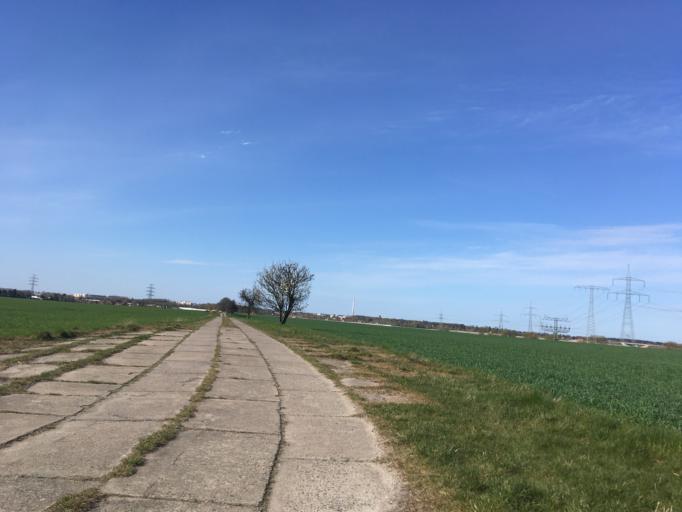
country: DE
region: Berlin
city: Karow
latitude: 52.6063
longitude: 13.5121
